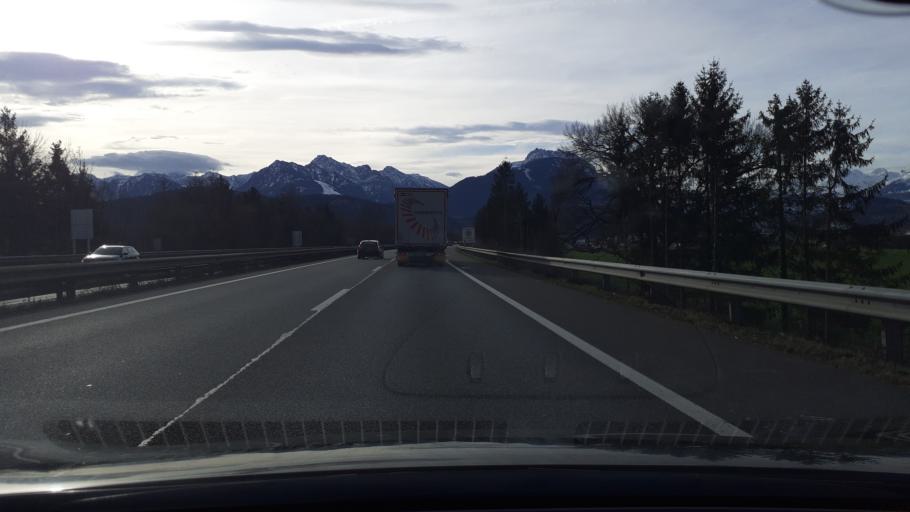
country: AT
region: Vorarlberg
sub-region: Politischer Bezirk Feldkirch
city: Rankweil
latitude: 47.2880
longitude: 9.6261
